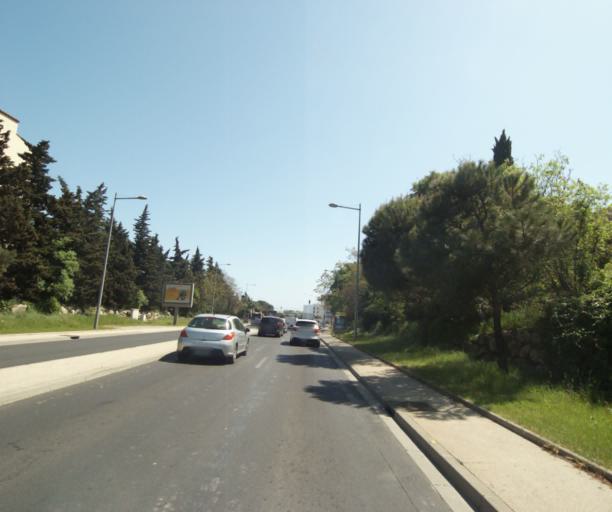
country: FR
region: Languedoc-Roussillon
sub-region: Departement de l'Herault
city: Montpellier
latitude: 43.5861
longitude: 3.8593
